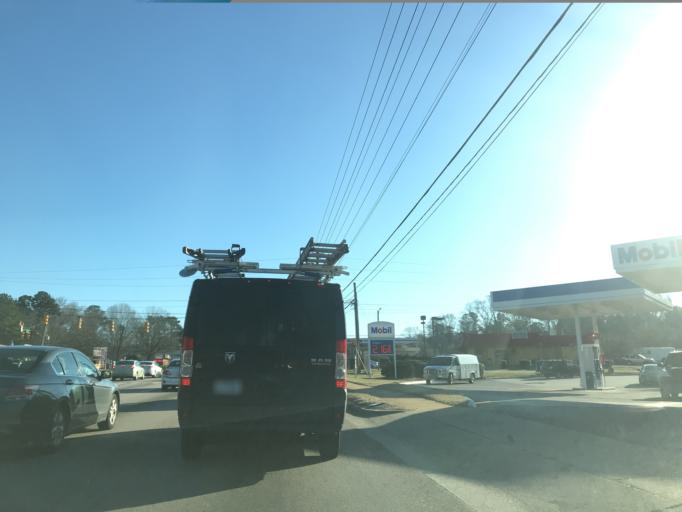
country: US
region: North Carolina
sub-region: Wake County
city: Raleigh
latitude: 35.7494
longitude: -78.6491
